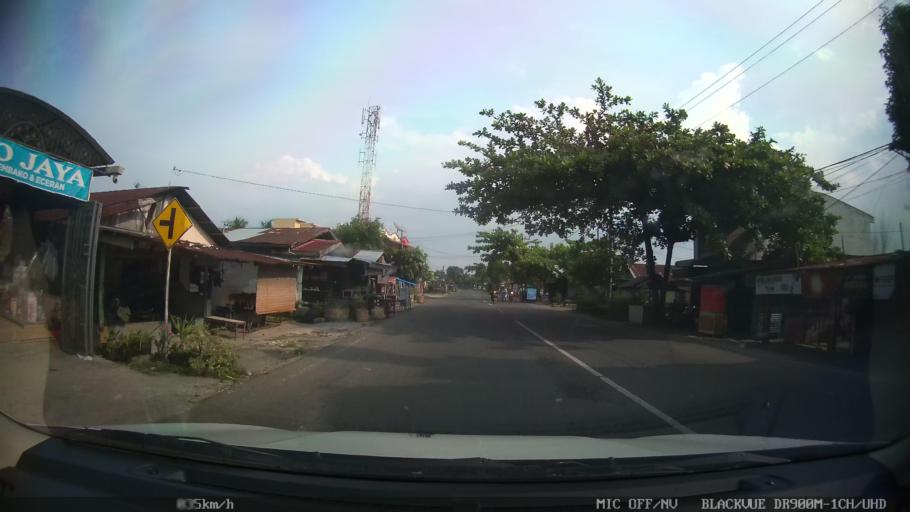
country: ID
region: North Sumatra
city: Binjai
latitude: 3.6033
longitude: 98.4958
